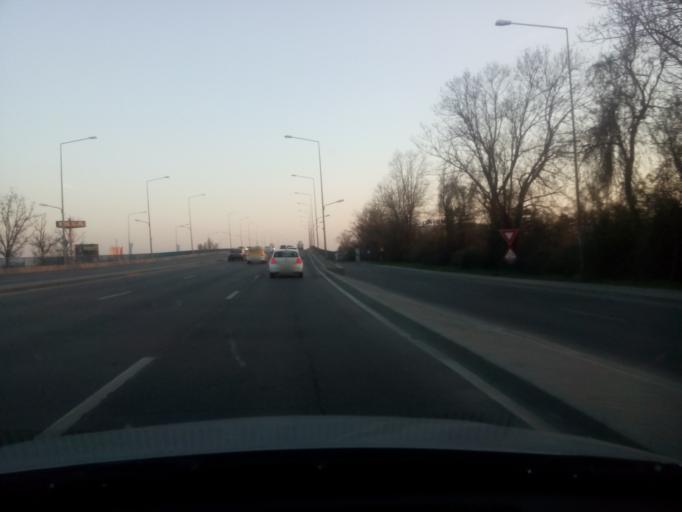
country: RO
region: Ilfov
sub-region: Comuna Otopeni
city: Otopeni
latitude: 44.5080
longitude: 26.0822
